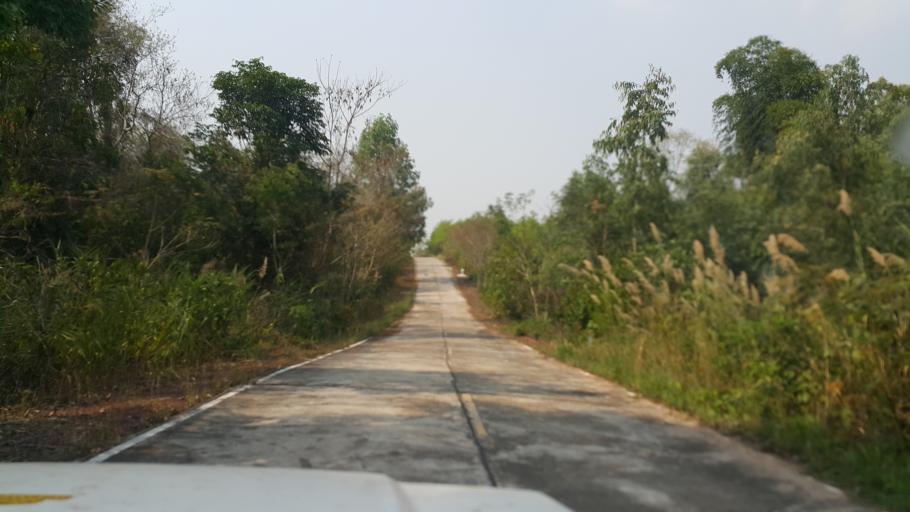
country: TH
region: Nakhon Phanom
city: Ban Phaeng
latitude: 17.9731
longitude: 104.1511
